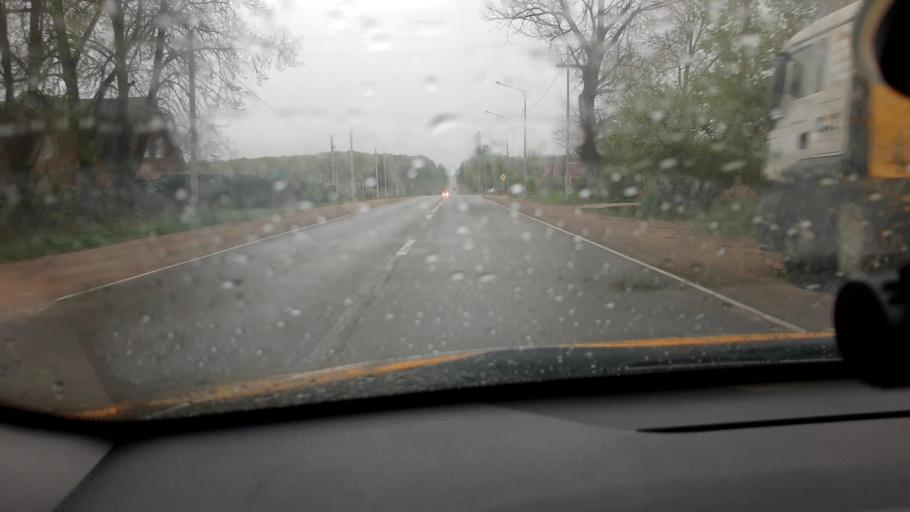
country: RU
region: Tula
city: Zaokskiy
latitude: 54.7448
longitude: 37.4394
